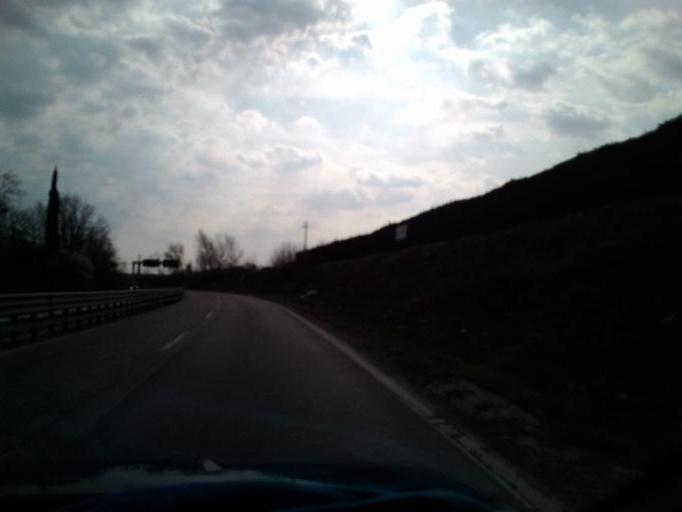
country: IT
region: Veneto
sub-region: Provincia di Verona
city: Pescantina
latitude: 45.4970
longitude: 10.8597
